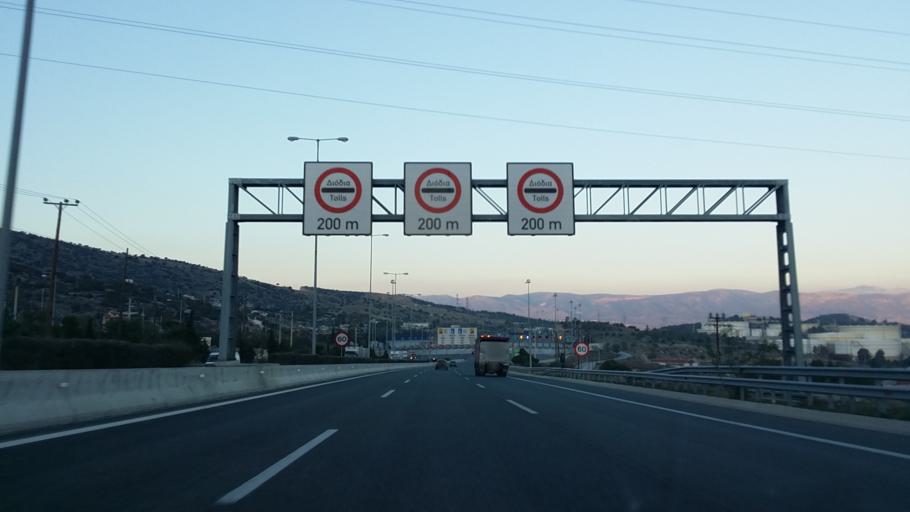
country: GR
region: Attica
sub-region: Nomarchia Dytikis Attikis
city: Mandra
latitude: 38.0367
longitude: 23.4921
